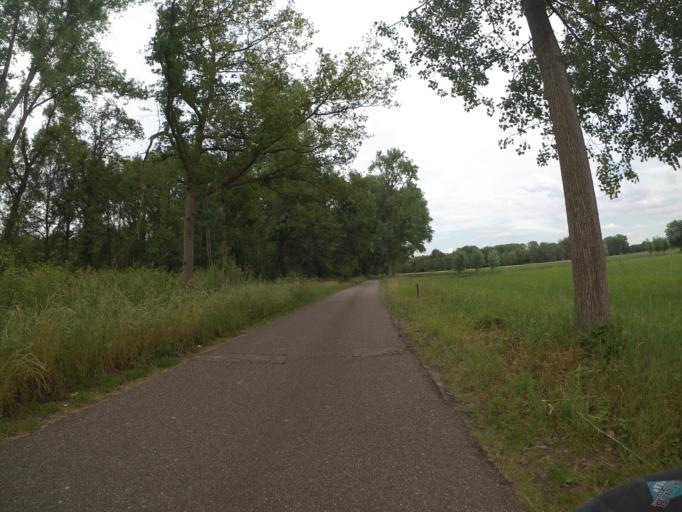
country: NL
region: North Brabant
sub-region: Gemeente Oirschot
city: Oirschot
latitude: 51.5285
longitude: 5.3482
